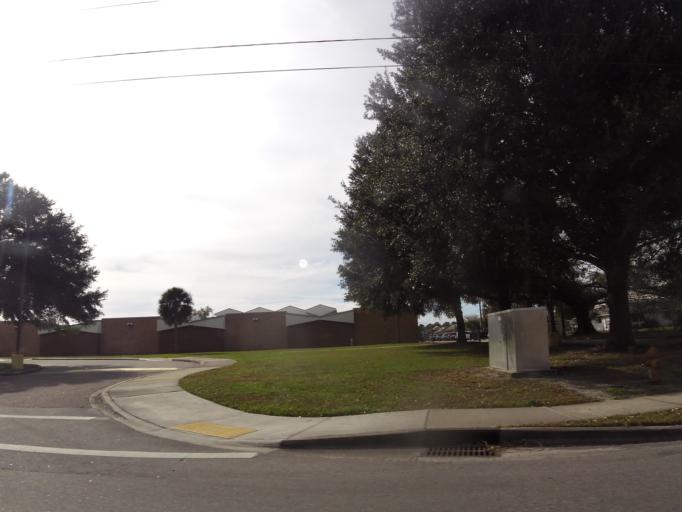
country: US
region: Florida
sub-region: Duval County
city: Jacksonville
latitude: 30.2523
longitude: -81.6153
